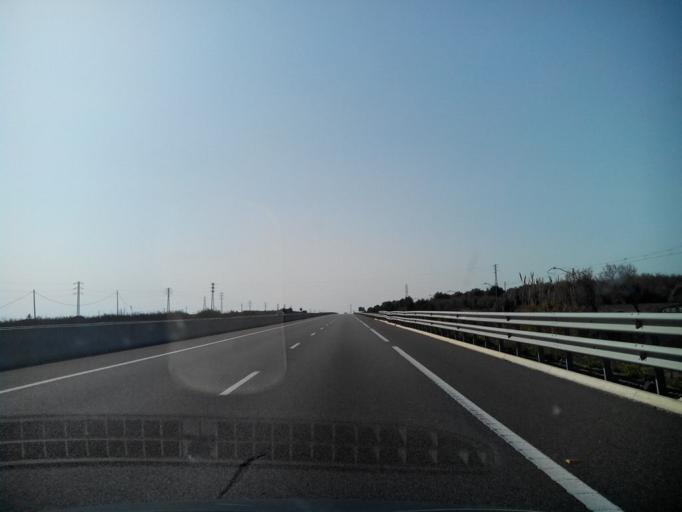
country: ES
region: Catalonia
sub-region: Provincia de Tarragona
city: Alcover
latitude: 41.2353
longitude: 1.1644
